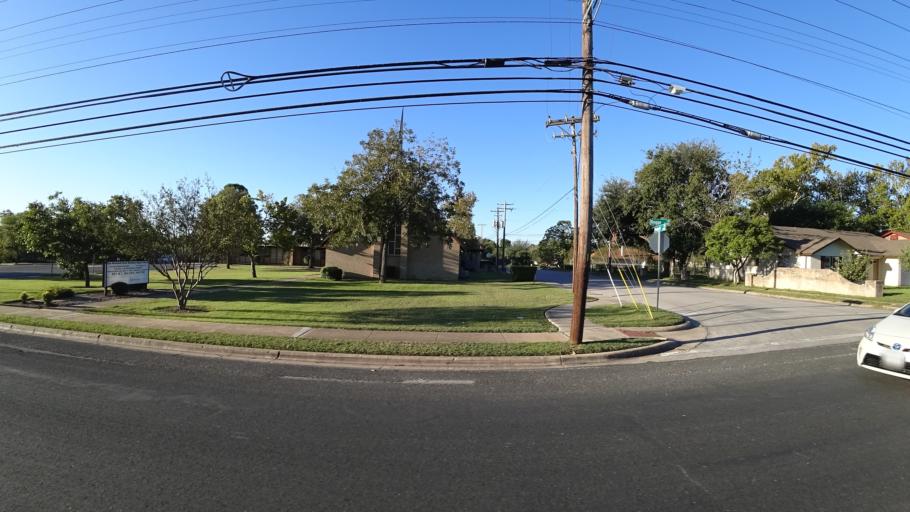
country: US
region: Texas
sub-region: Travis County
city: Austin
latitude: 30.3023
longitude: -97.6766
